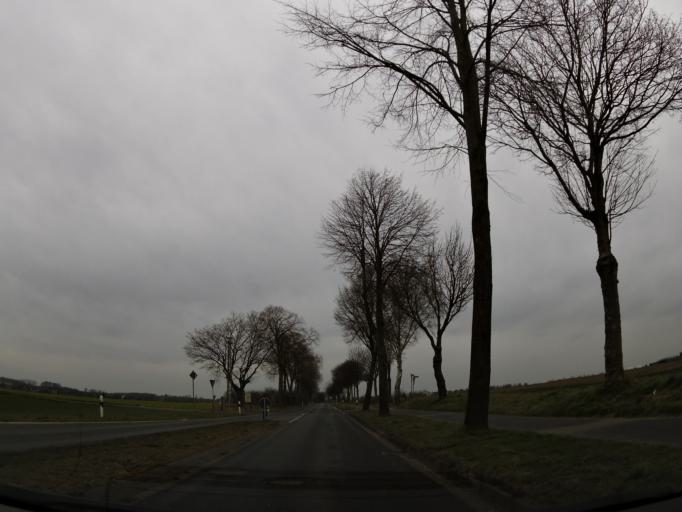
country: NL
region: Limburg
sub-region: Gemeente Schinnen
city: Doenrade
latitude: 50.9955
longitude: 5.9132
